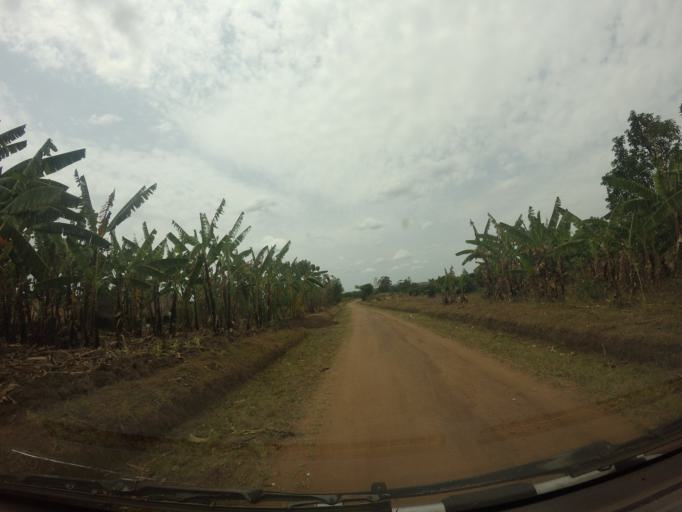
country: UG
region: Northern Region
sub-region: Arua District
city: Arua
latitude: 2.8201
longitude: 30.9011
